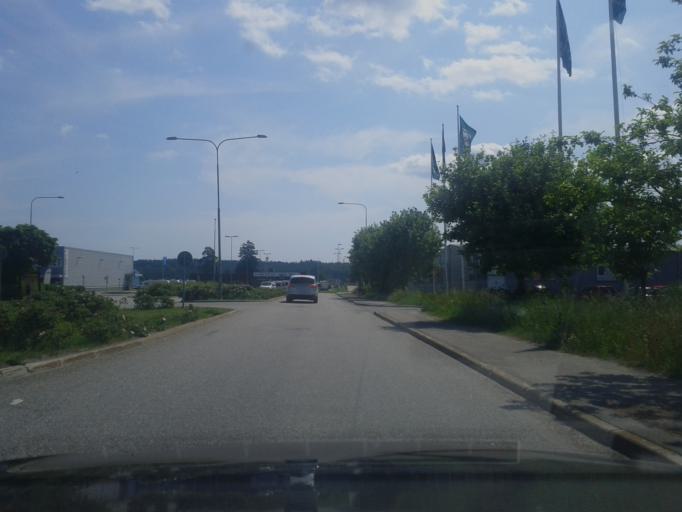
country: SE
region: Stockholm
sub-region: Taby Kommun
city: Taby
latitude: 59.4609
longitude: 18.1355
